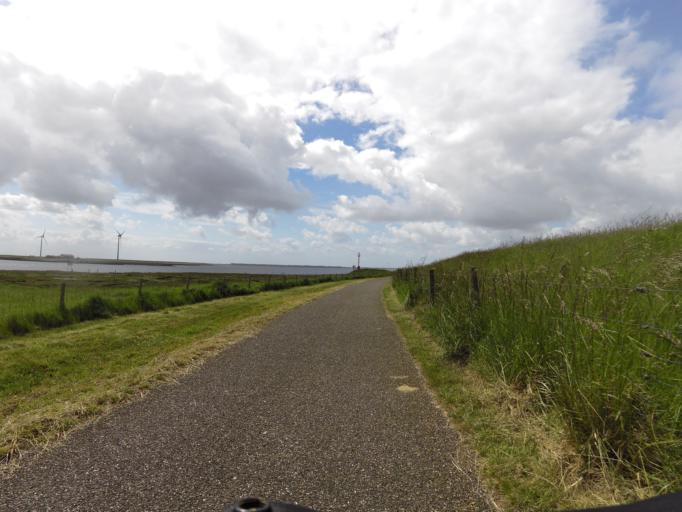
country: NL
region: Zeeland
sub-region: Schouwen-Duiveland
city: Bruinisse
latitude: 51.6480
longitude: 4.0954
